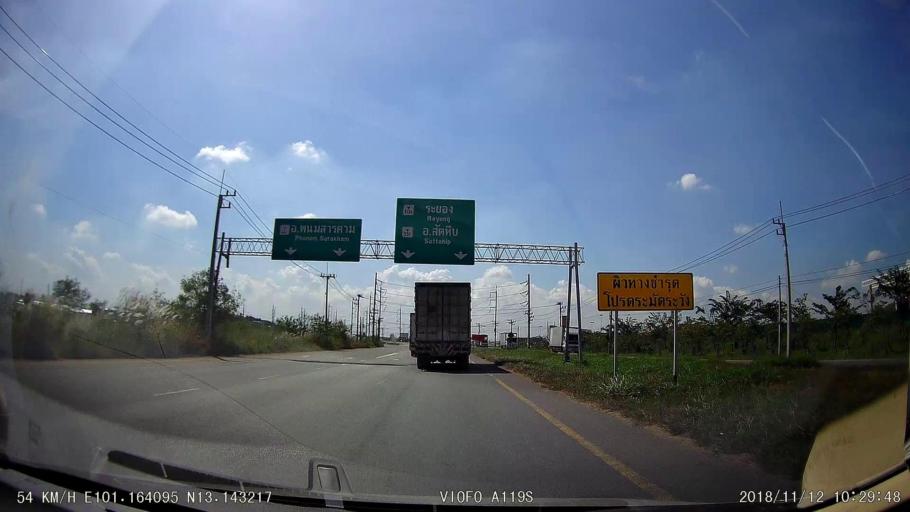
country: TH
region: Rayong
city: Pluak Daeng
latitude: 13.1340
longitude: 101.1668
